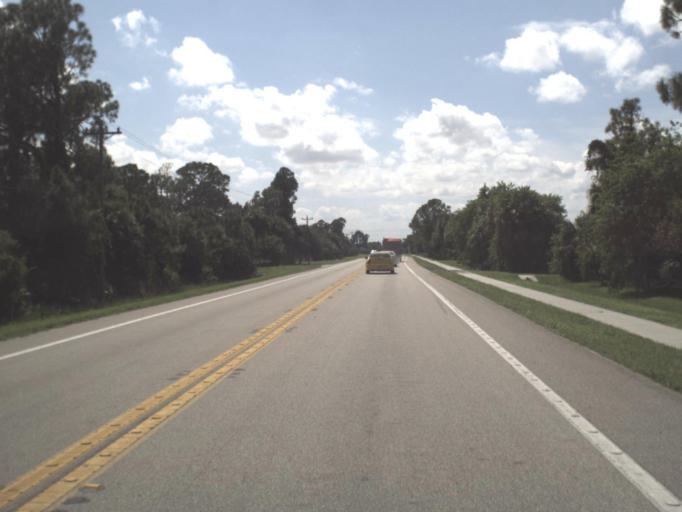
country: US
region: Florida
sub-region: Collier County
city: Immokalee
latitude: 26.5481
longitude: -81.4357
